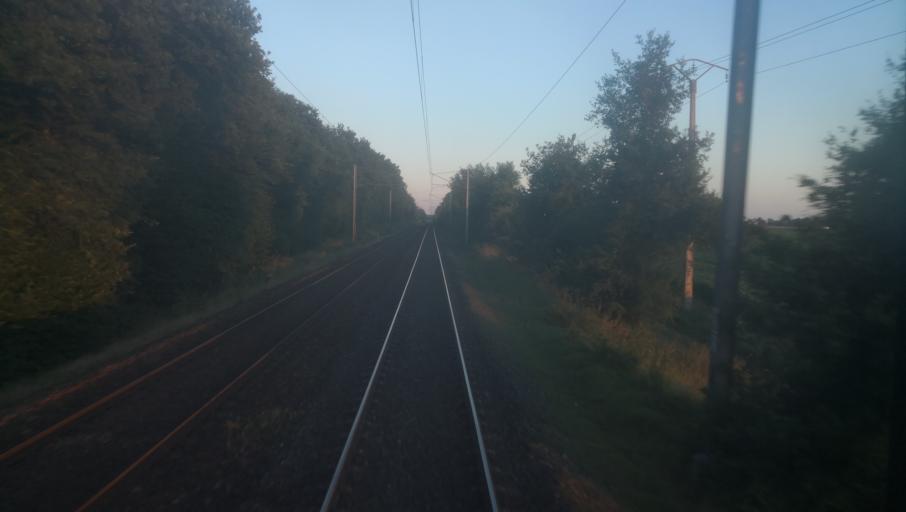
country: FR
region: Bourgogne
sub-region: Departement de la Nievre
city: Pouilly-sur-Loire
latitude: 47.2568
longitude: 2.9983
